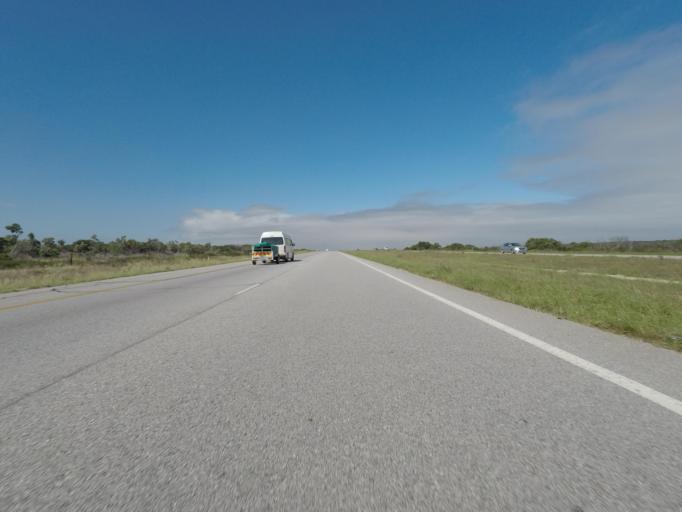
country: ZA
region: Eastern Cape
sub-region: Nelson Mandela Bay Metropolitan Municipality
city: Port Elizabeth
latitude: -33.7461
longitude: 25.7221
